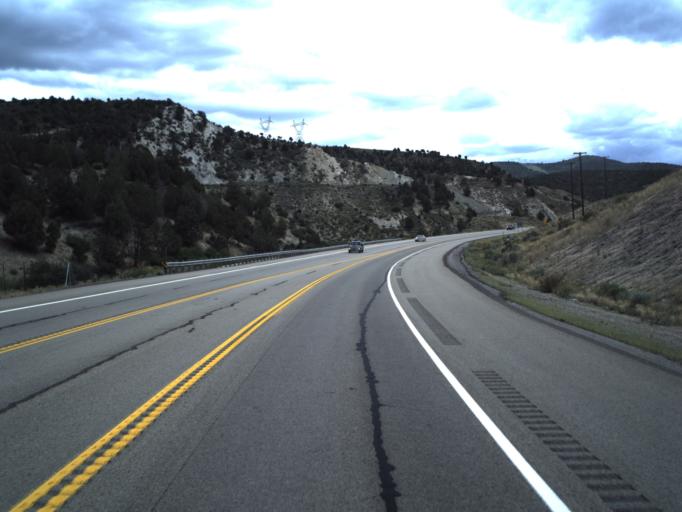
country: US
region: Utah
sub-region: Sanpete County
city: Fairview
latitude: 39.9404
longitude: -111.1997
